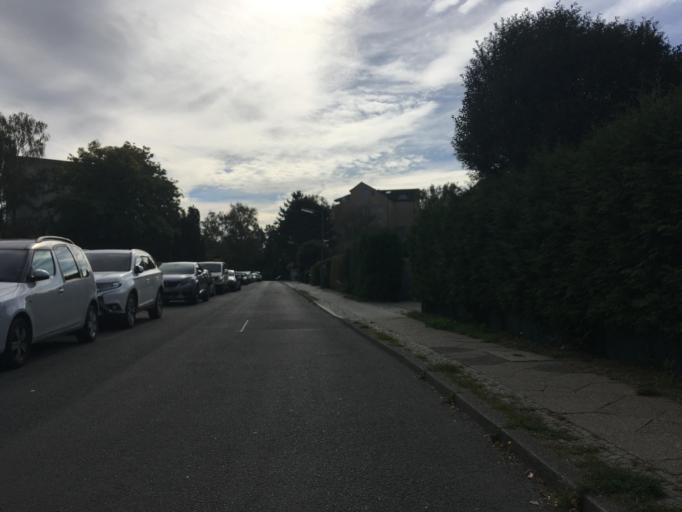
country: DE
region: Berlin
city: Britz
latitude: 52.4258
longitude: 13.4297
